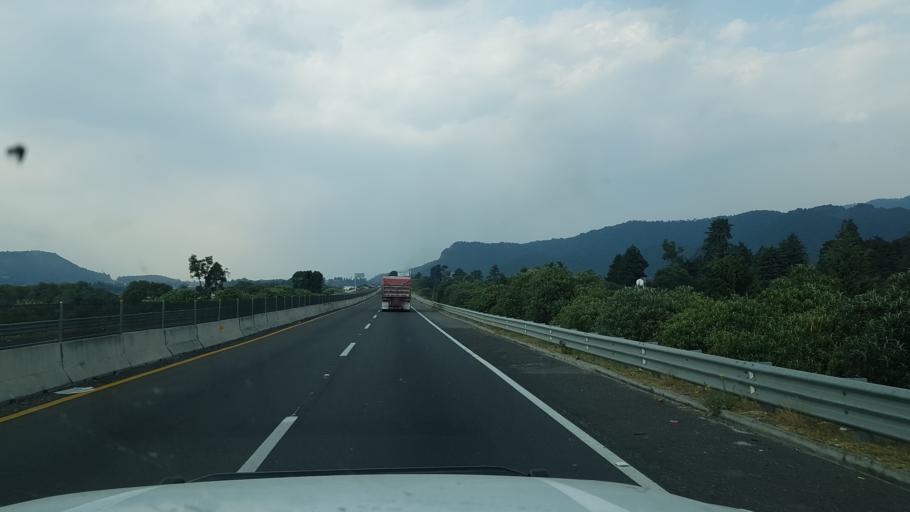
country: MX
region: Mexico
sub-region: Ayapango
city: La Colonia
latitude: 19.1413
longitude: -98.7760
